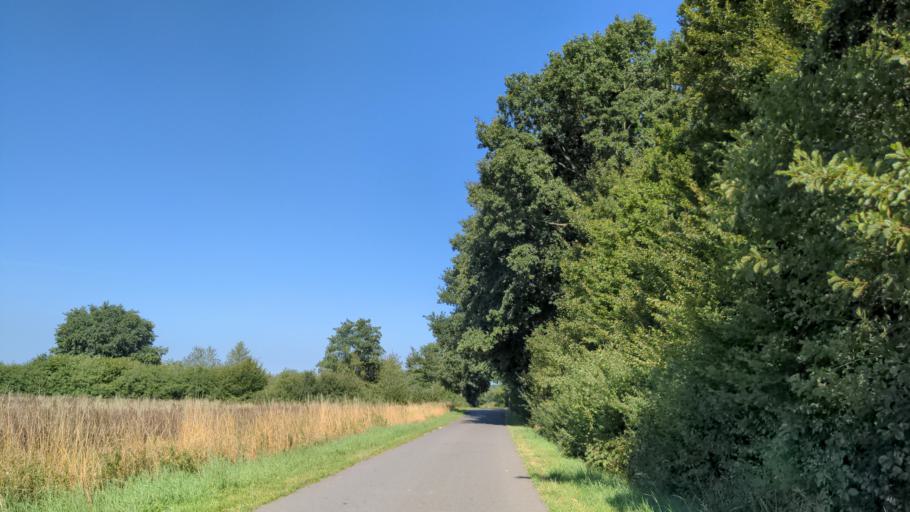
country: DE
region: Schleswig-Holstein
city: Klempau
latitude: 53.7644
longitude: 10.6760
